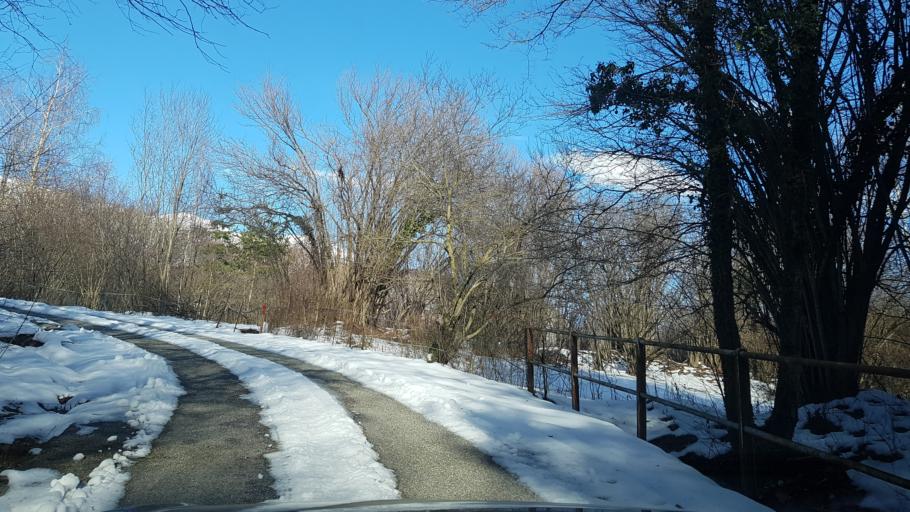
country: IT
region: Friuli Venezia Giulia
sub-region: Provincia di Udine
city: Trasaghis
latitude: 46.2941
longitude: 13.0304
